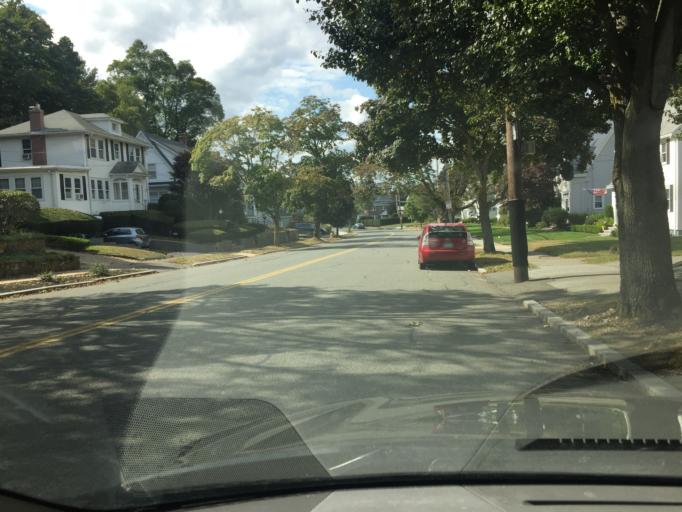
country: US
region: Massachusetts
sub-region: Middlesex County
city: Medford
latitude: 42.4251
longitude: -71.1137
